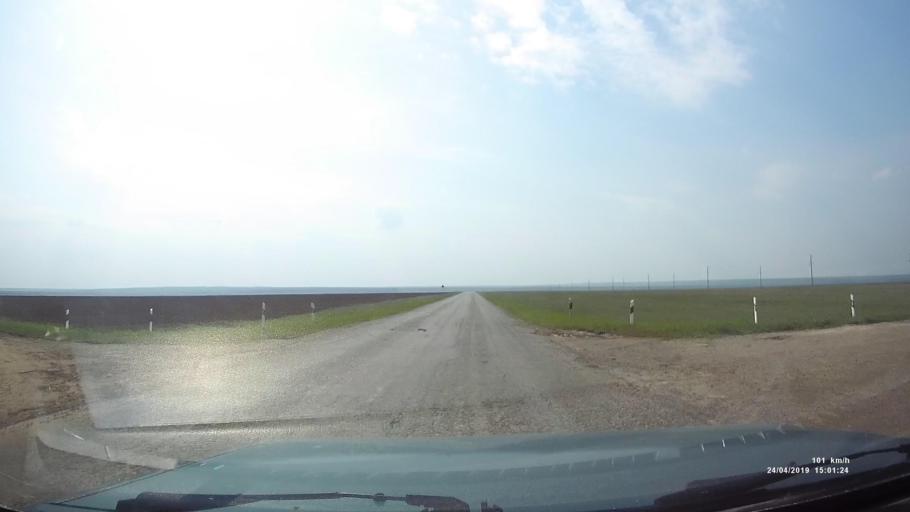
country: RU
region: Rostov
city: Remontnoye
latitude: 46.5660
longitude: 43.5342
